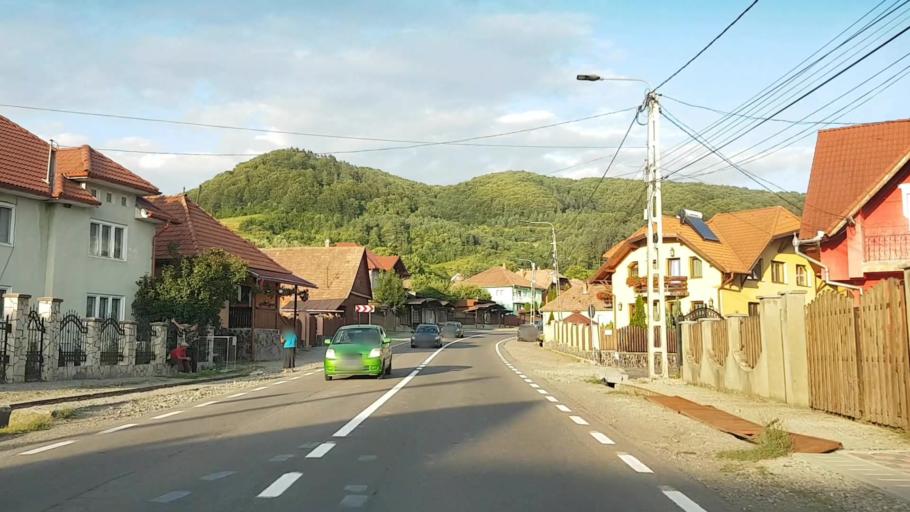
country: RO
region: Harghita
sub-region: Comuna Corund
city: Corund
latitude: 46.4697
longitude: 25.1962
